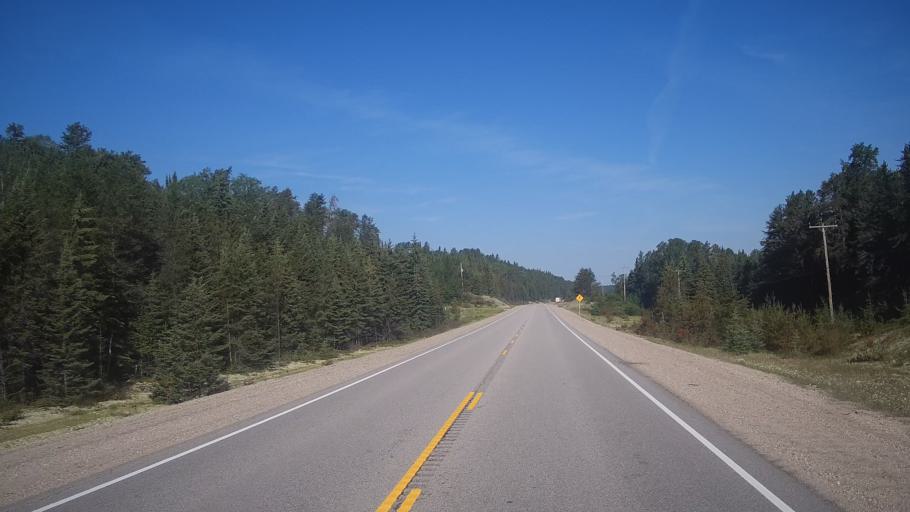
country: CA
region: Ontario
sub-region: Rainy River District
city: Atikokan
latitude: 49.4649
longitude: -91.9056
